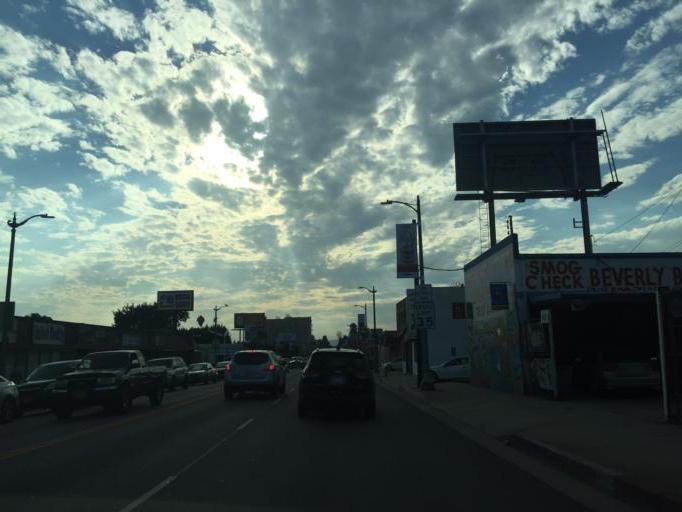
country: US
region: California
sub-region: Los Angeles County
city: Hollywood
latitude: 34.0763
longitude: -118.3046
